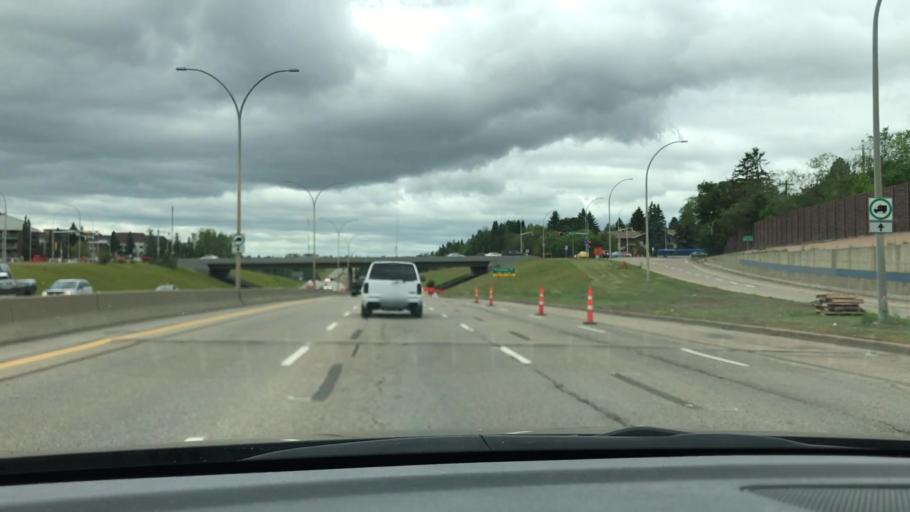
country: CA
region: Alberta
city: Edmonton
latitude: 53.4832
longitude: -113.5383
